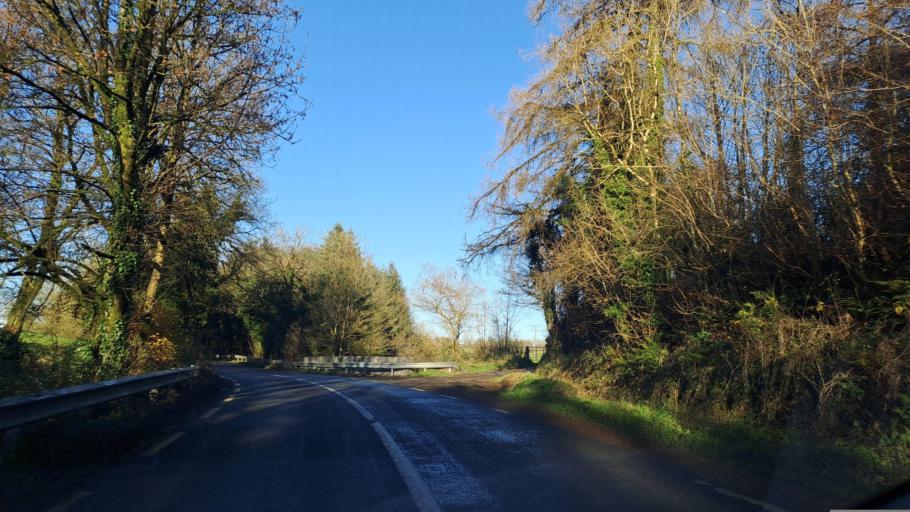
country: IE
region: Ulster
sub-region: An Cabhan
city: Mullagh
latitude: 53.8587
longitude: -6.9548
